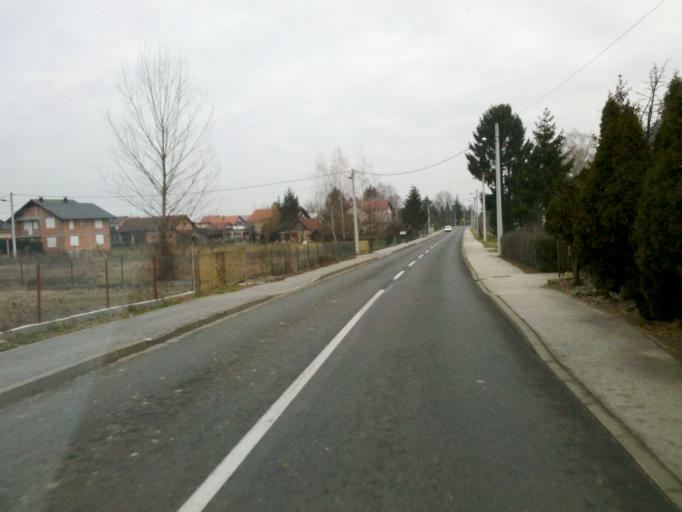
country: HR
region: Grad Zagreb
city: Strmec
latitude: 45.6769
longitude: 15.8743
